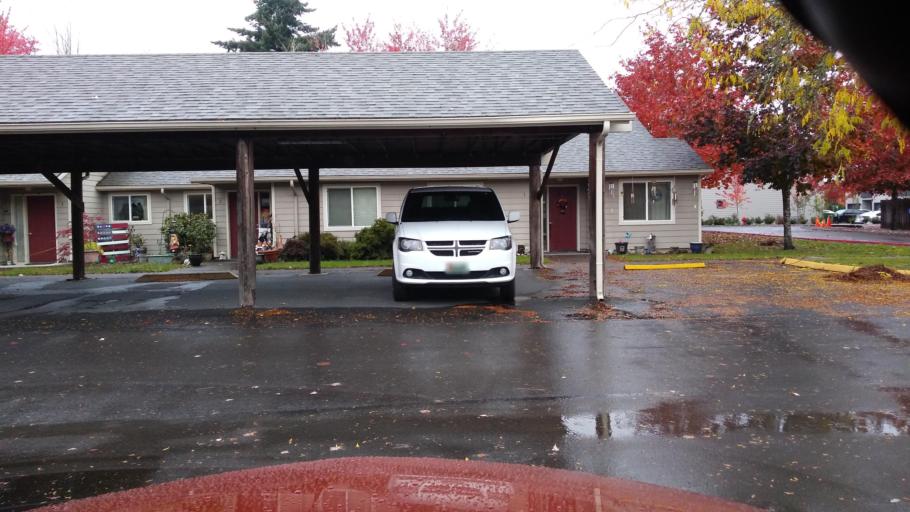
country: US
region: Oregon
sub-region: Washington County
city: Forest Grove
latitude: 45.5216
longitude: -123.0952
